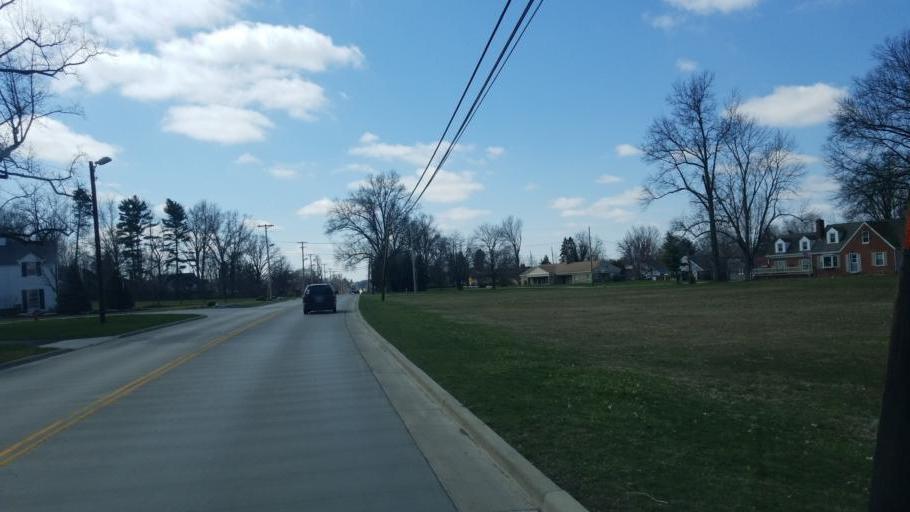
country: US
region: Ohio
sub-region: Crawford County
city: Galion
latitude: 40.7295
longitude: -82.8039
